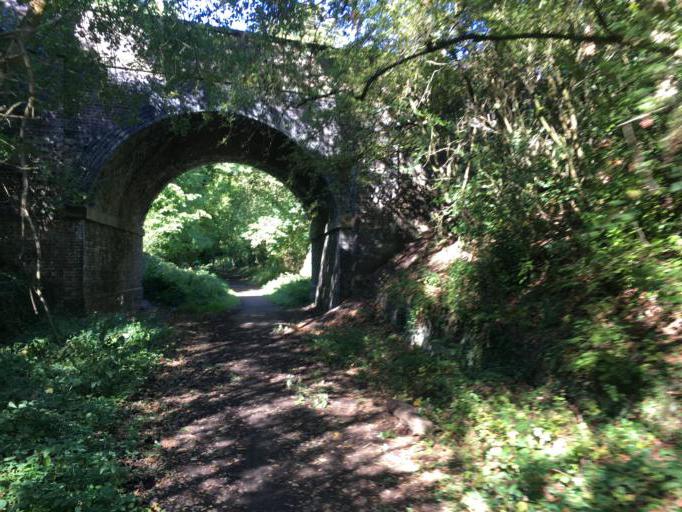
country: GB
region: England
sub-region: Warwickshire
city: Kenilworth
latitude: 52.3804
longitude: -1.6059
